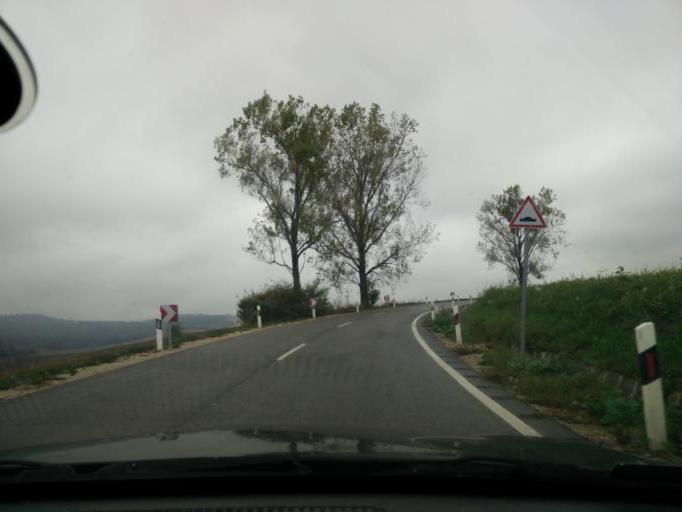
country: HU
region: Komarom-Esztergom
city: Bajna
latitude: 47.6394
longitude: 18.5710
